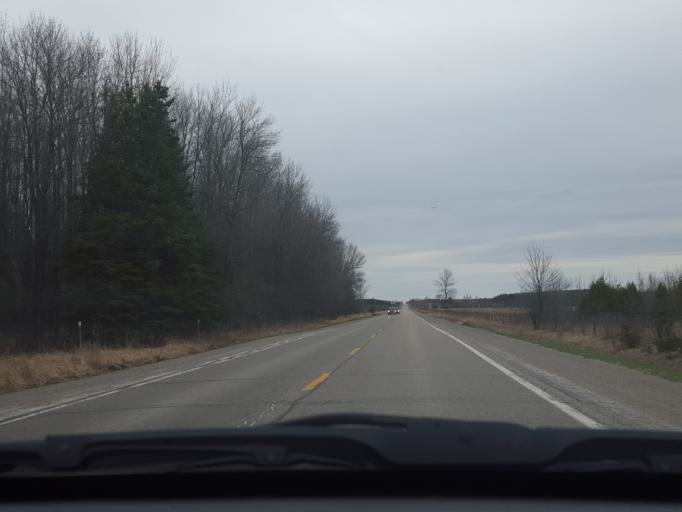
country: CA
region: Ontario
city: Uxbridge
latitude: 44.2998
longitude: -79.1723
